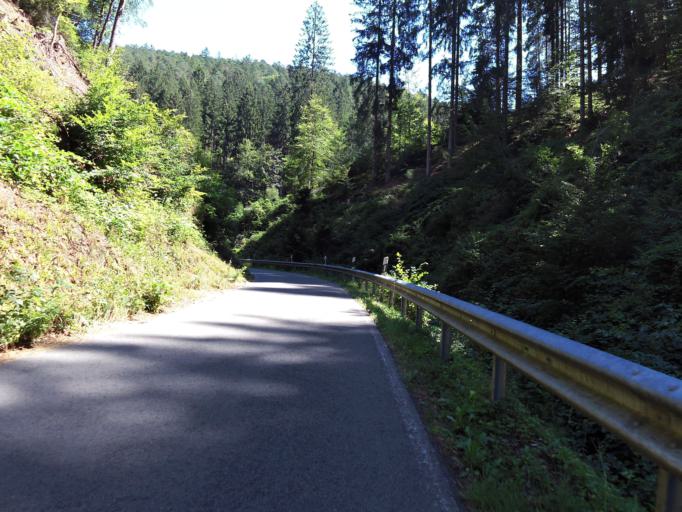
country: DE
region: Rheinland-Pfalz
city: Elmstein
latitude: 49.3769
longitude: 7.9198
